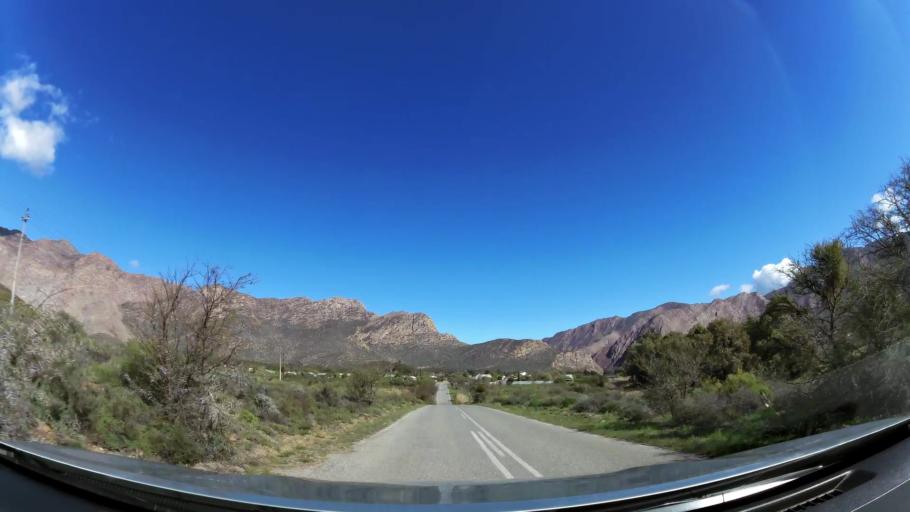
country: ZA
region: Western Cape
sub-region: Cape Winelands District Municipality
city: Ashton
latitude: -33.7905
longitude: 20.1305
